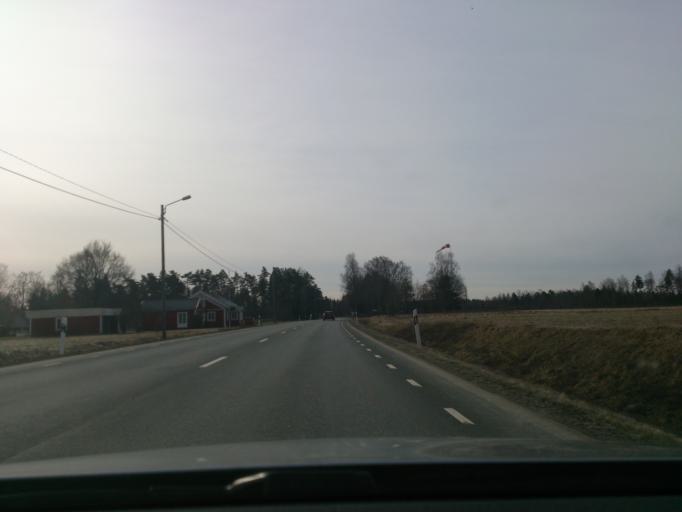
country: SE
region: Kronoberg
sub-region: Alvesta Kommun
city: Moheda
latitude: 56.9798
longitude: 14.5678
